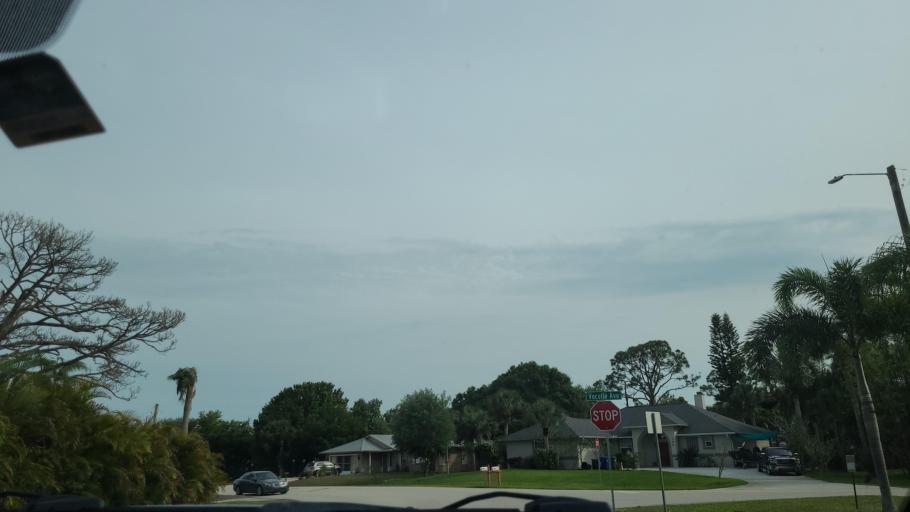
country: US
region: Florida
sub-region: Indian River County
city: Sebastian
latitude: 27.7929
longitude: -80.4865
